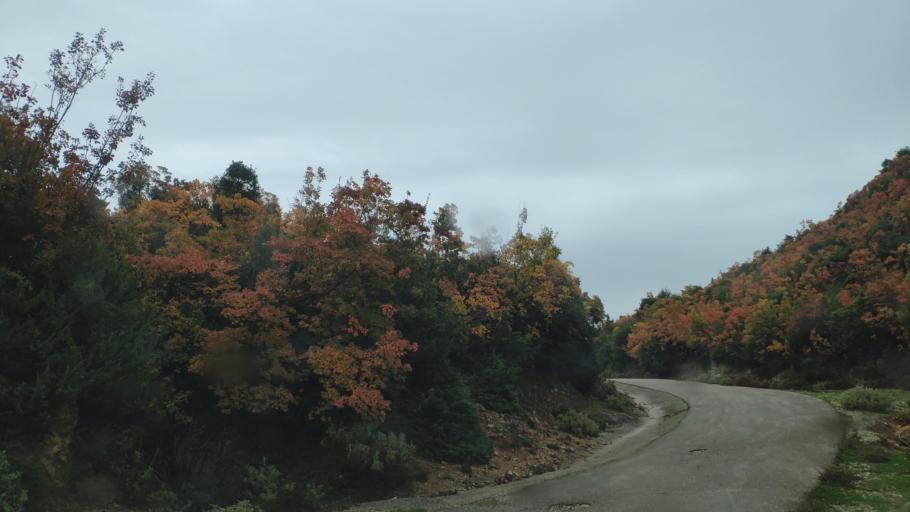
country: GR
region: Epirus
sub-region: Nomos Prevezis
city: Kanalaki
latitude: 39.3382
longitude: 20.6536
